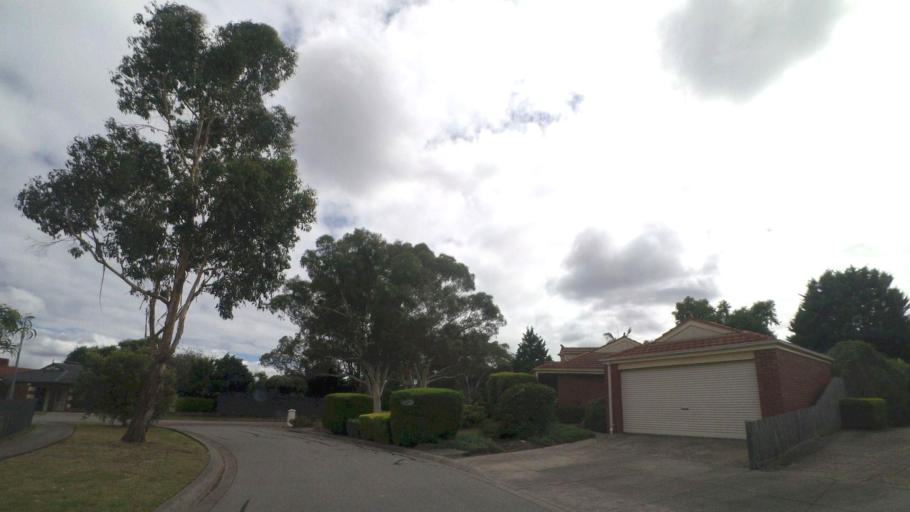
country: AU
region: Victoria
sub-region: Maroondah
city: Bayswater North
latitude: -37.8325
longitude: 145.3068
